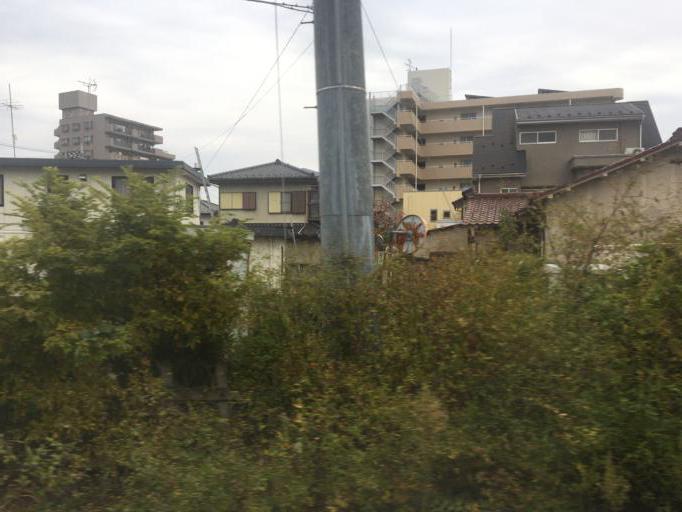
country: JP
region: Saitama
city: Hanno
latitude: 35.8506
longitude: 139.3262
